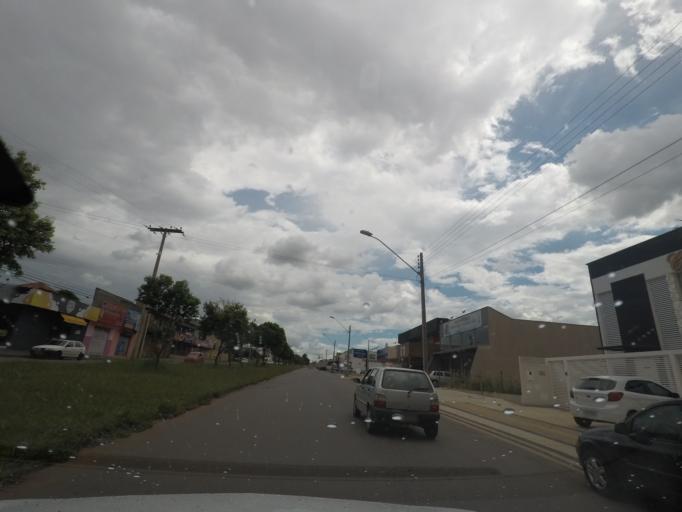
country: BR
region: Goias
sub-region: Goiania
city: Goiania
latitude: -16.7307
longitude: -49.3409
